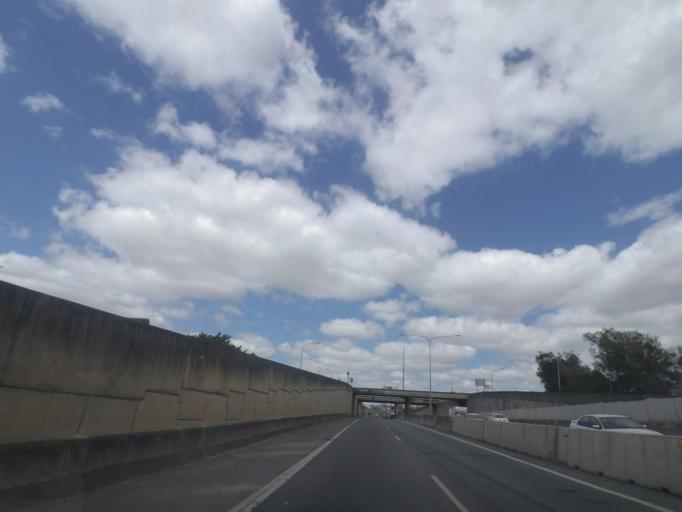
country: AU
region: Queensland
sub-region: Brisbane
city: Seventeen Mile Rocks
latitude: -27.5661
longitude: 152.9813
